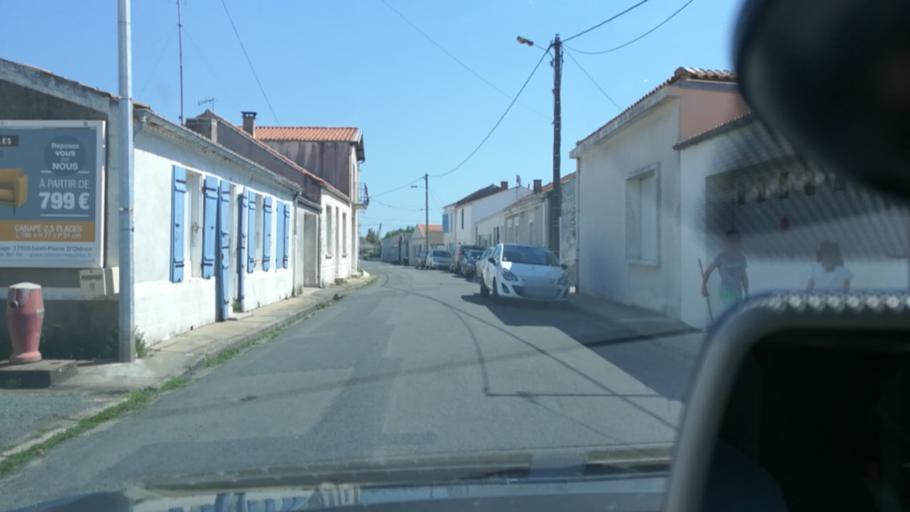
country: FR
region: Poitou-Charentes
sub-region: Departement de la Charente-Maritime
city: Saint-Trojan-les-Bains
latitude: 45.8737
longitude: -1.2161
